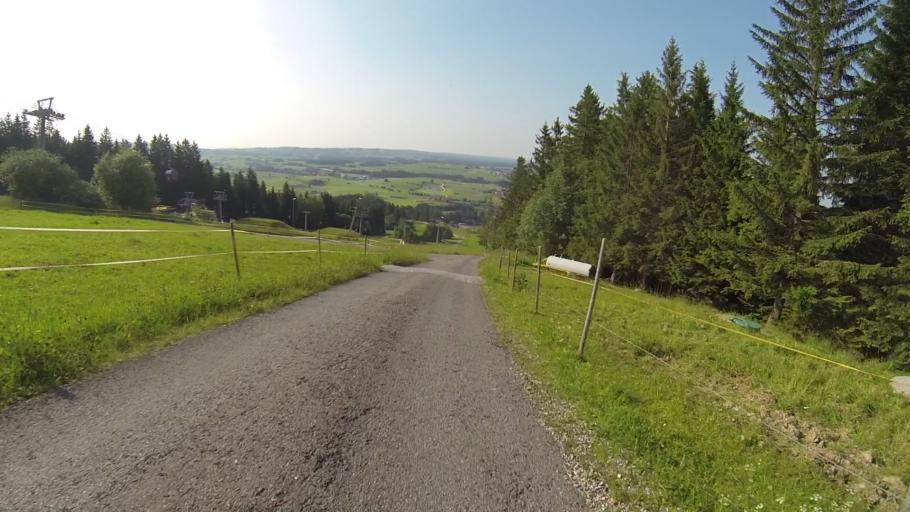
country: DE
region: Bavaria
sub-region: Swabia
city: Nesselwang
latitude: 47.6110
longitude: 10.4982
